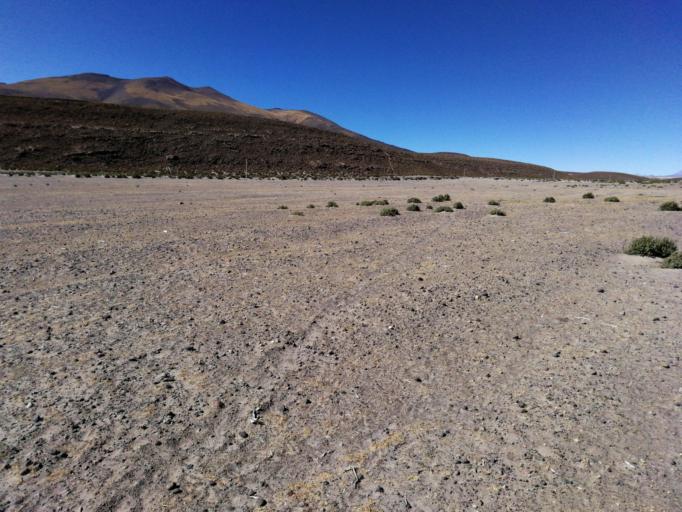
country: BO
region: Oruro
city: Cruz de Machacamarca
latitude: -19.2627
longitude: -68.3203
